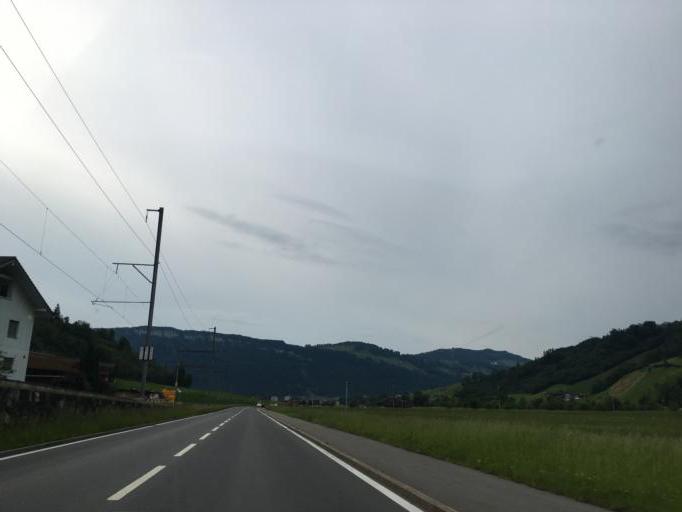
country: CH
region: Nidwalden
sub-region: Nidwalden
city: Dallenwil
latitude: 46.9363
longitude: 8.3917
